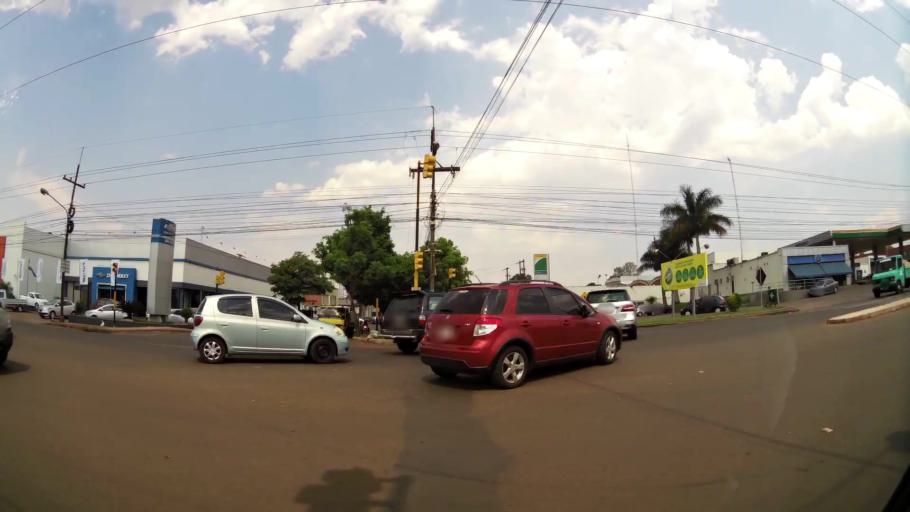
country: PY
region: Alto Parana
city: Ciudad del Este
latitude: -25.4979
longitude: -54.6349
